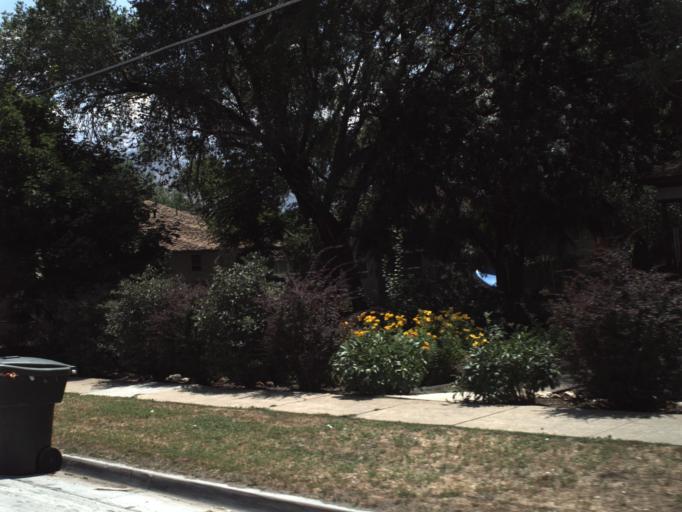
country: US
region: Utah
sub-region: Weber County
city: Ogden
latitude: 41.2442
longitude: -111.9679
